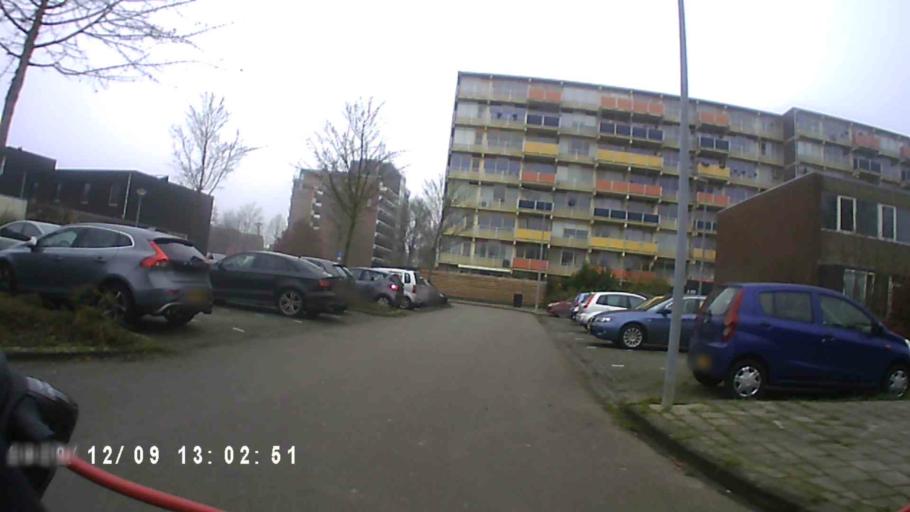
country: NL
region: Groningen
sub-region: Gemeente Groningen
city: Oosterpark
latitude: 53.2368
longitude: 6.6272
